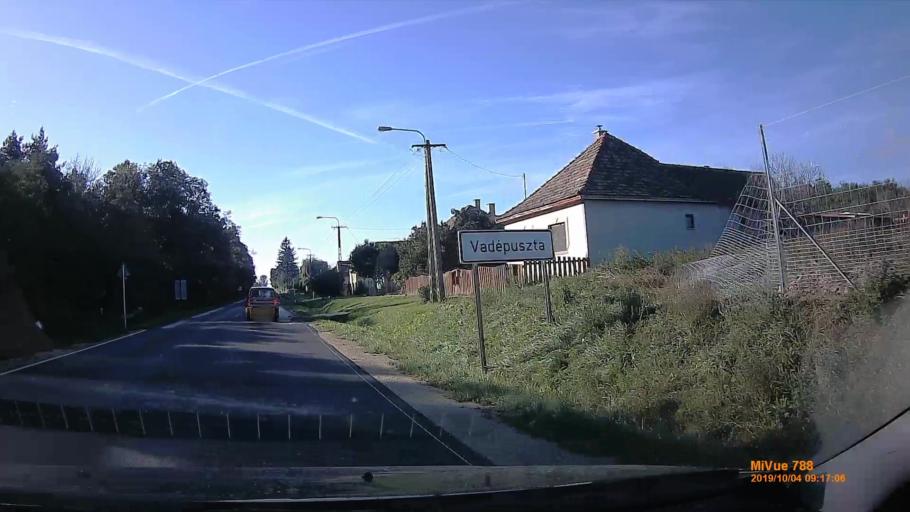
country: HU
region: Somogy
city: Karad
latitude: 46.6054
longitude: 17.7992
